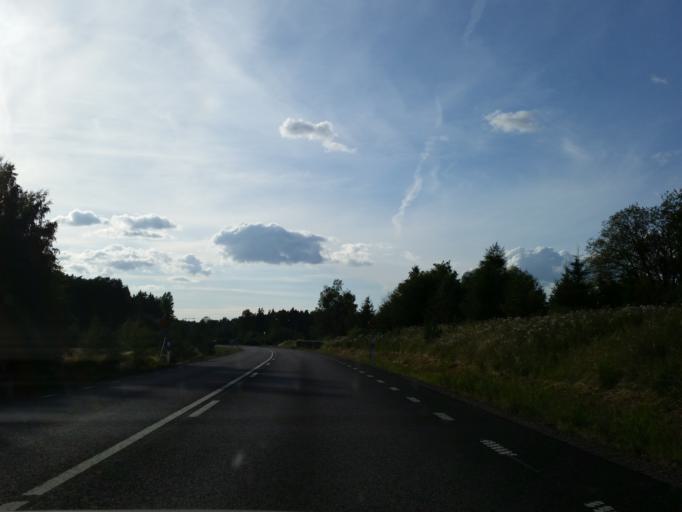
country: SE
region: Soedermanland
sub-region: Gnesta Kommun
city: Gnesta
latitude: 59.0467
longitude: 17.2863
